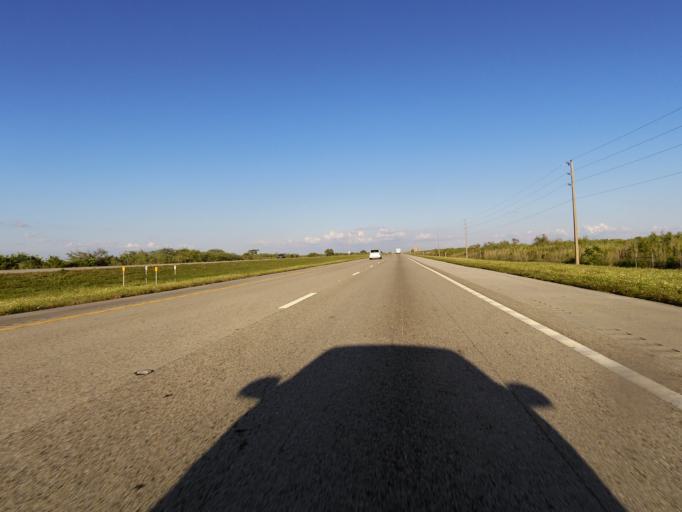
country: US
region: Florida
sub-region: Broward County
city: Weston
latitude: 26.1556
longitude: -80.7600
